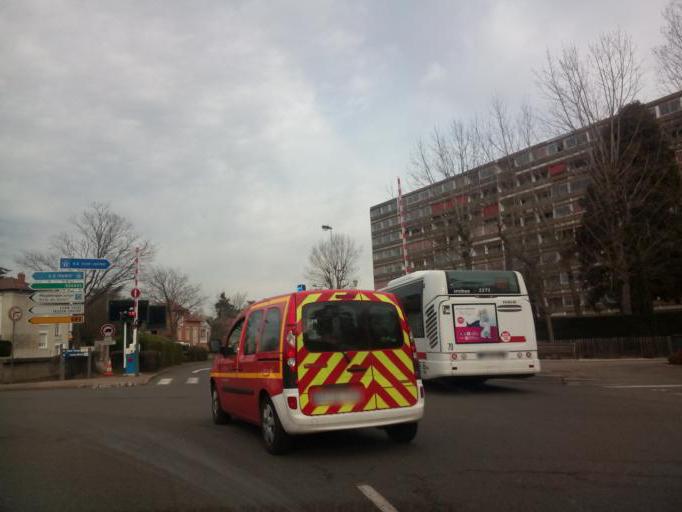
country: FR
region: Rhone-Alpes
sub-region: Departement du Rhone
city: Tassin-la-Demi-Lune
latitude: 45.7643
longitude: 4.7861
